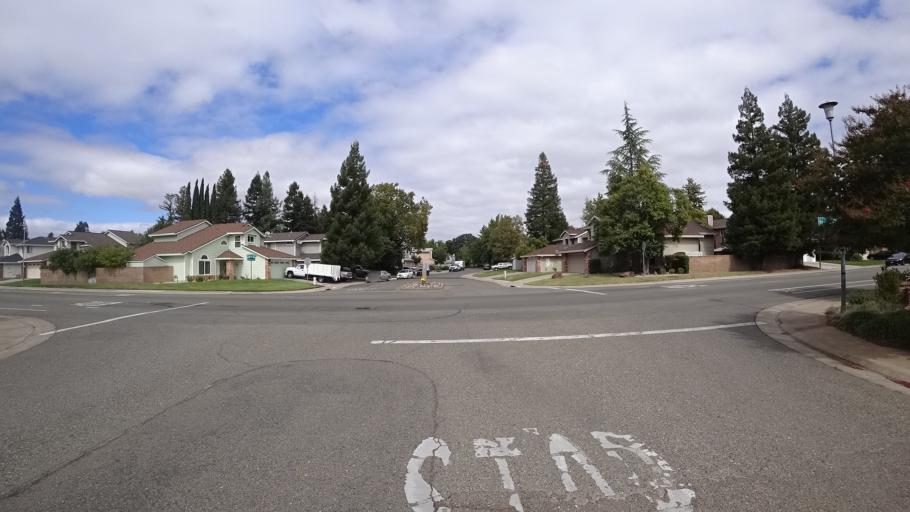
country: US
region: California
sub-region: Sacramento County
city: Laguna
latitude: 38.4179
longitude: -121.4357
